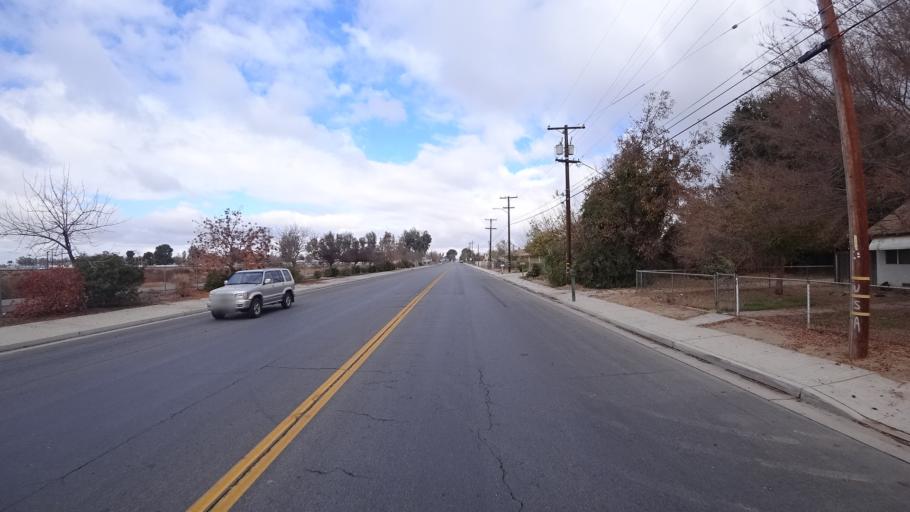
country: US
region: California
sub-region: Kern County
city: Bakersfield
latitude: 35.3351
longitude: -118.9942
